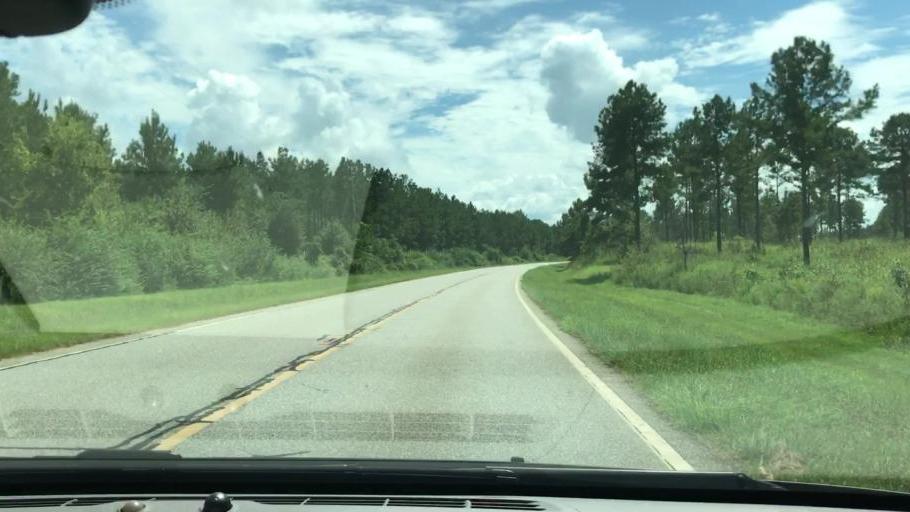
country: US
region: Georgia
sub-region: Quitman County
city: Georgetown
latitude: 32.0705
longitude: -85.0365
